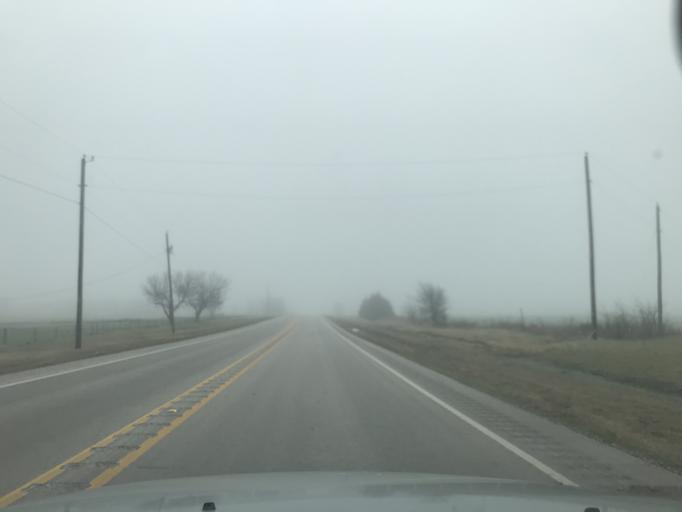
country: US
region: Texas
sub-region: Rockwall County
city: Royse City
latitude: 33.0013
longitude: -96.3007
